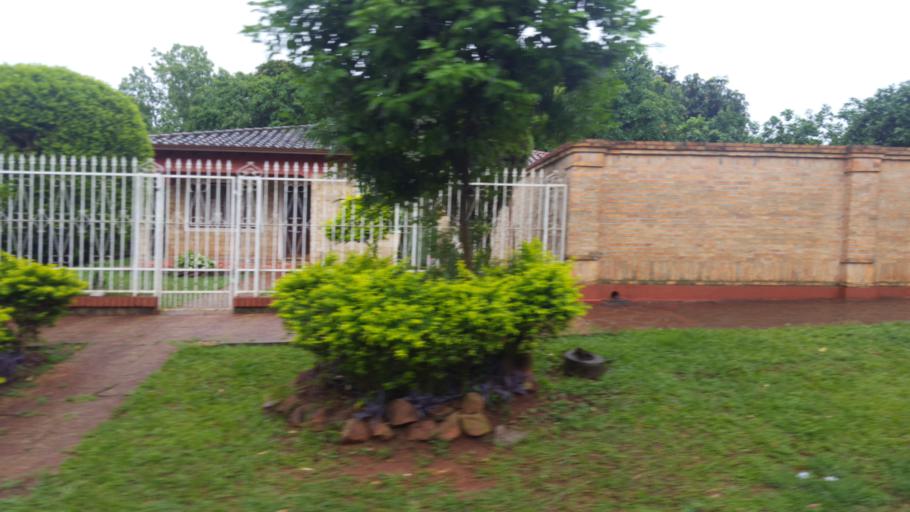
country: PY
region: Misiones
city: San Juan Bautista
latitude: -26.6696
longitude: -57.1502
